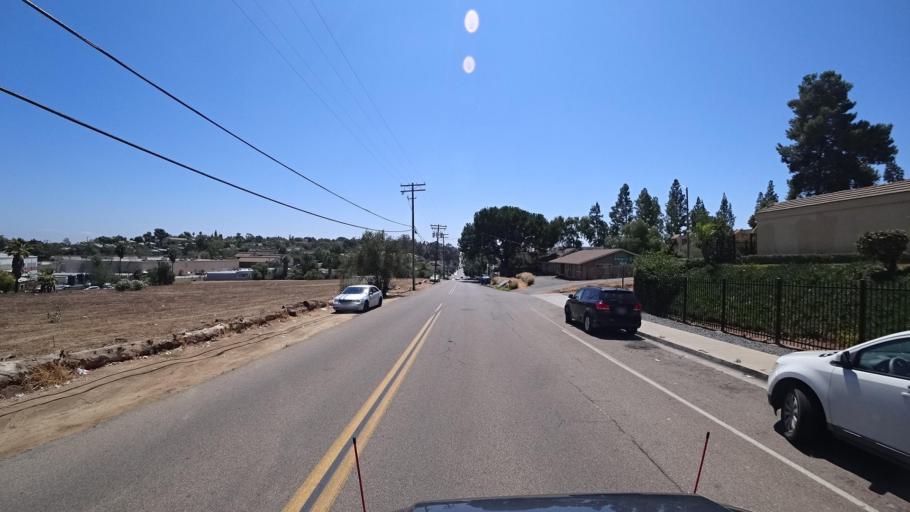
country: US
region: California
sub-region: San Diego County
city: Fallbrook
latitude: 33.3735
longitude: -117.2580
